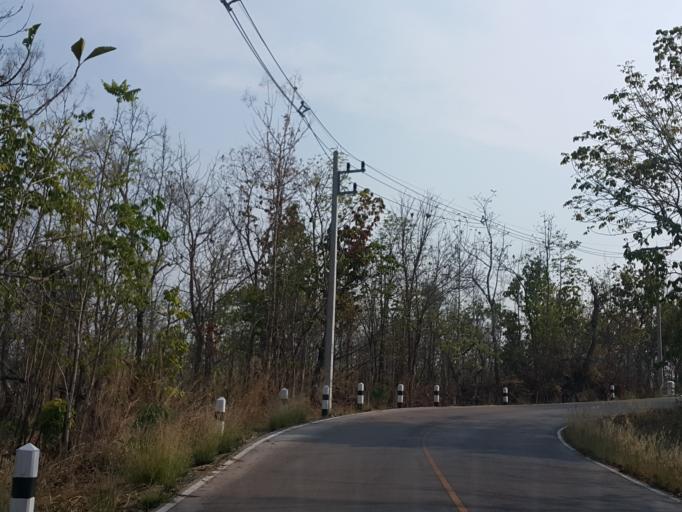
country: TH
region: Lampang
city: Chae Hom
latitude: 18.7423
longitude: 99.5480
